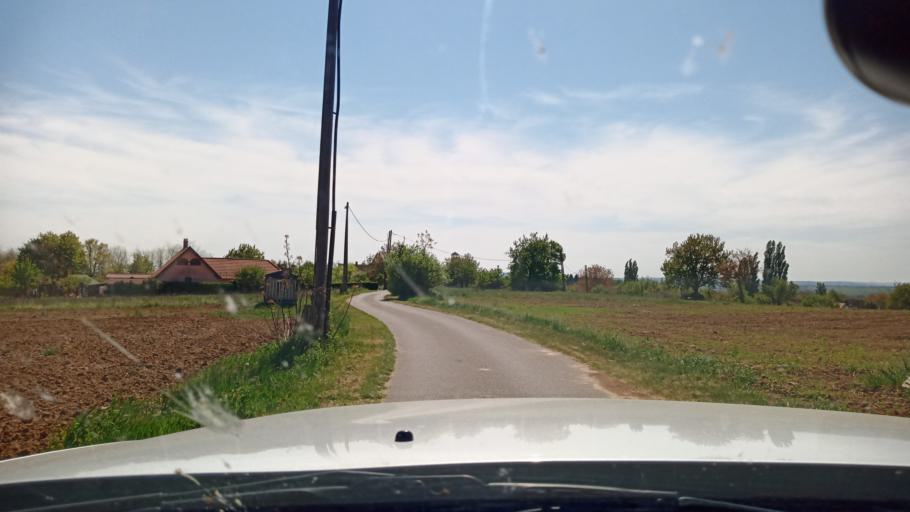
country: HU
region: Zala
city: Heviz
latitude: 46.7640
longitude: 17.1471
